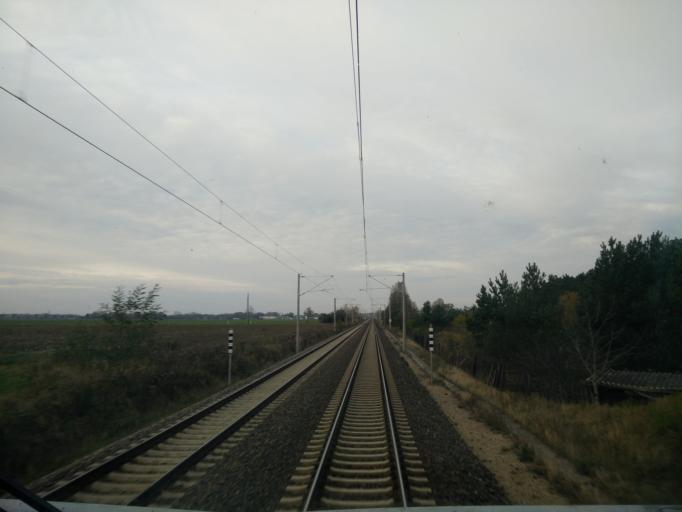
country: DE
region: Brandenburg
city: Luebben
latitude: 51.9172
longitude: 13.8968
